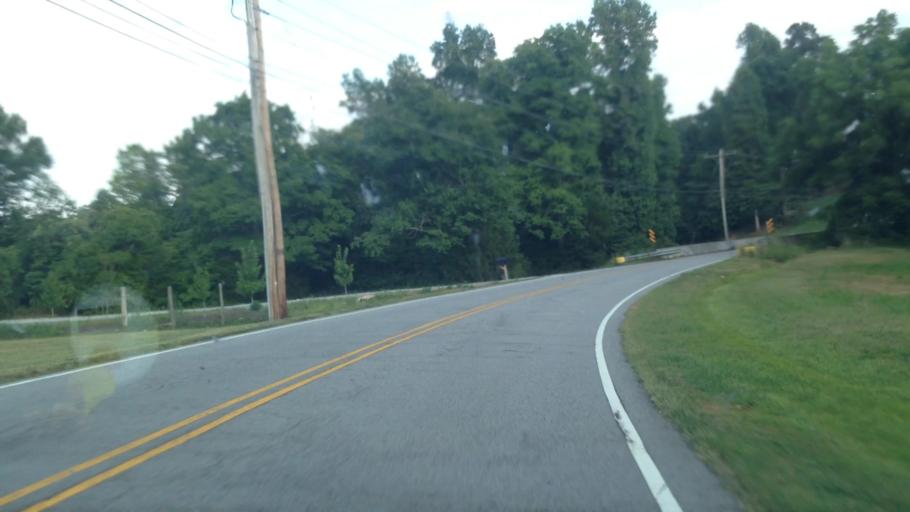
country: US
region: North Carolina
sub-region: Davidson County
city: Wallburg
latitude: 35.9655
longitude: -80.0795
